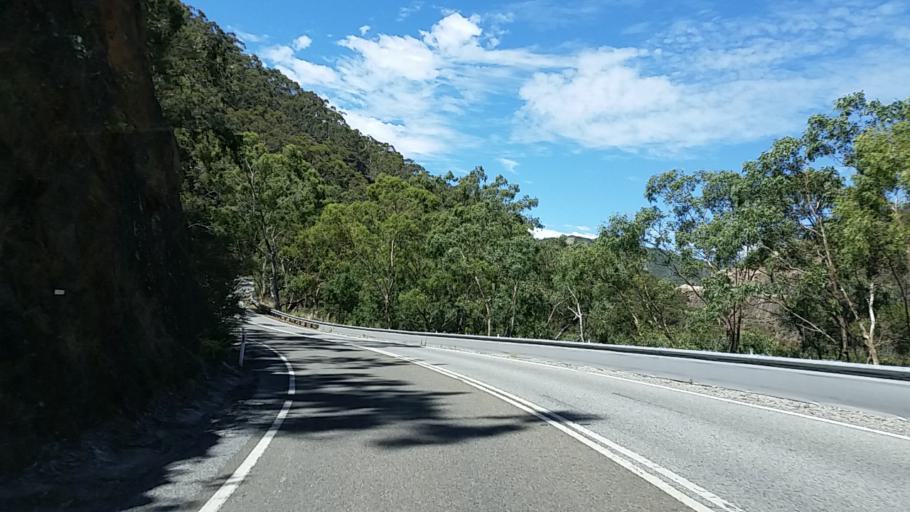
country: AU
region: South Australia
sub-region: Campbelltown
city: Athelstone
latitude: -34.8646
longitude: 138.7667
